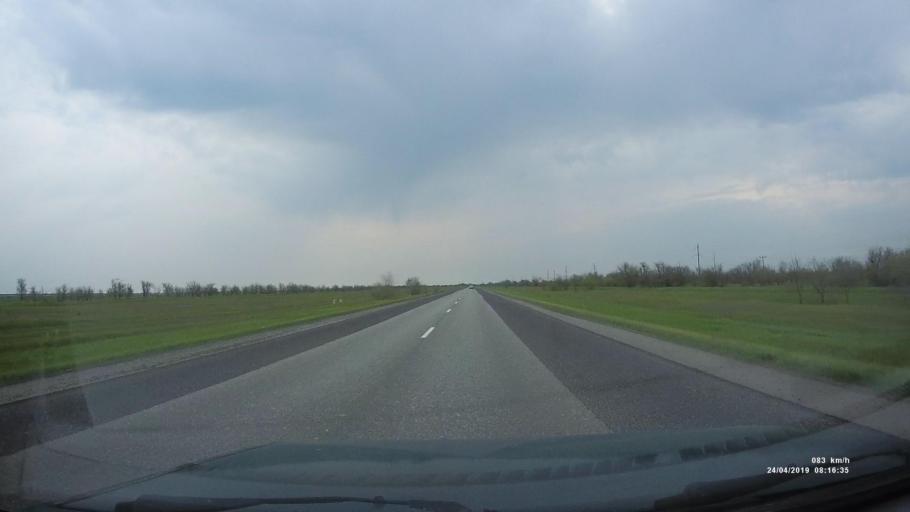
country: RU
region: Kalmykiya
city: Priyutnoye
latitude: 46.0988
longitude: 43.6147
